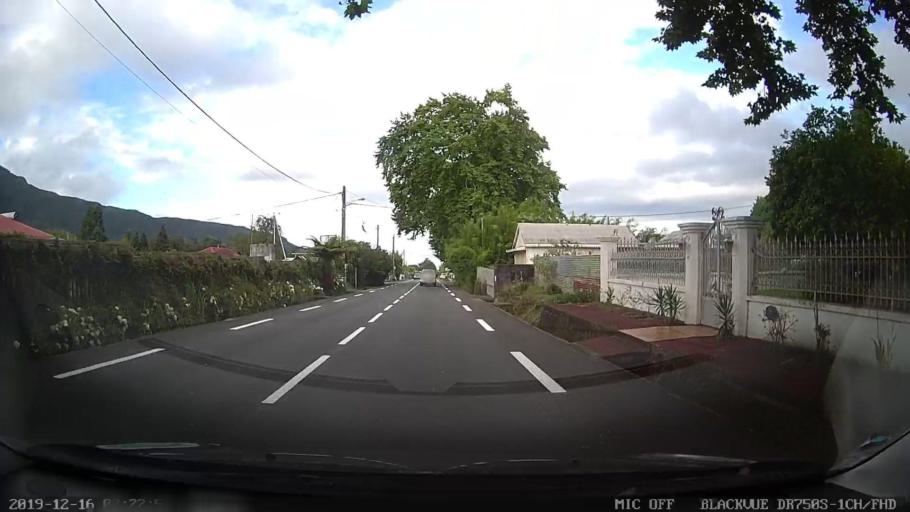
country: RE
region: Reunion
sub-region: Reunion
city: Salazie
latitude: -21.1455
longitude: 55.6184
